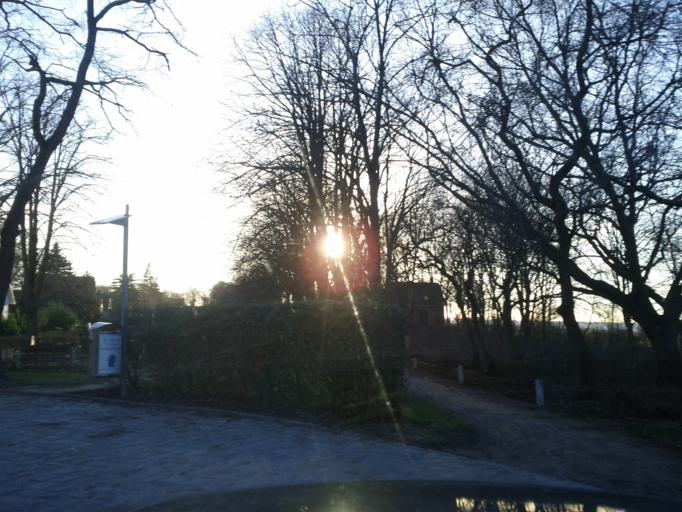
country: DE
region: Mecklenburg-Vorpommern
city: Blowatz
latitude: 54.0148
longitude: 11.4291
